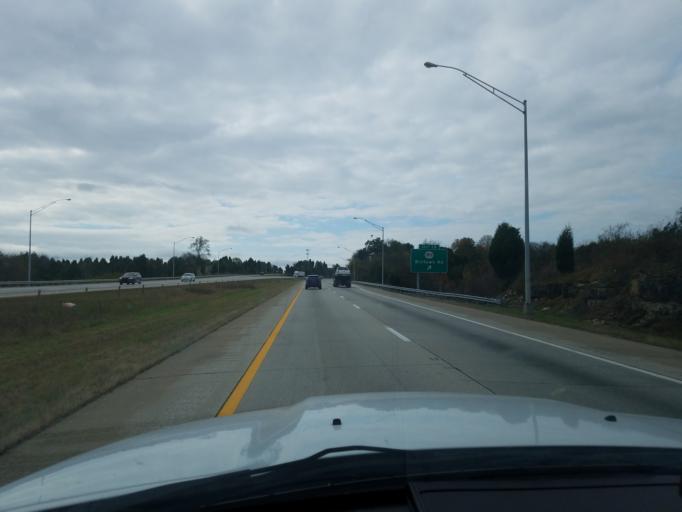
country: US
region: Kentucky
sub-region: Jefferson County
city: Fern Creek
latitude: 38.1499
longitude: -85.5396
